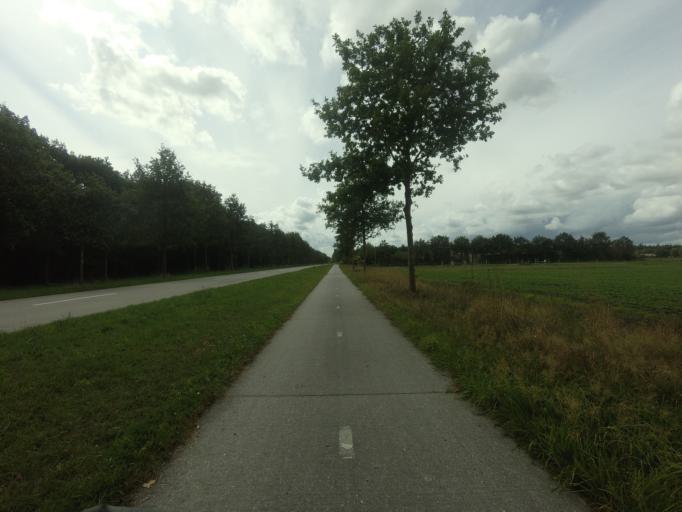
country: NL
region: Groningen
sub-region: Gemeente Leek
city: Leek
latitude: 53.0272
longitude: 6.4157
